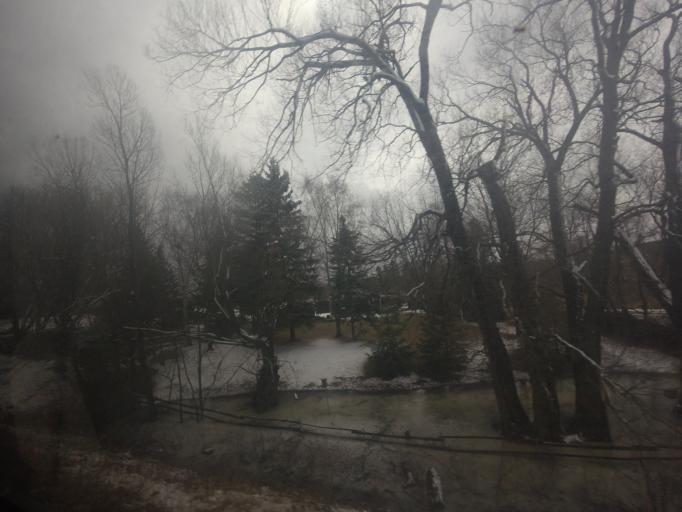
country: CA
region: Ontario
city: Cobourg
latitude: 43.9440
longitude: -78.3379
